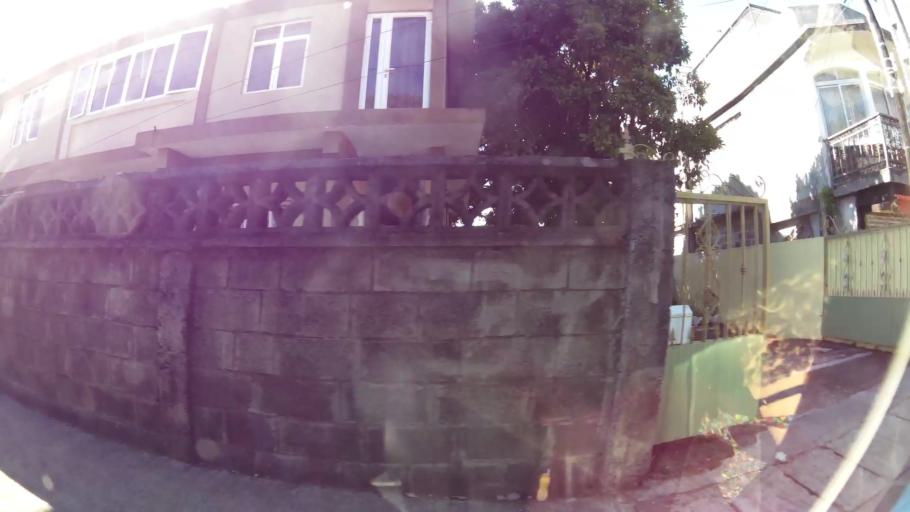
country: MU
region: Plaines Wilhems
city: Vacoas
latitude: -20.3242
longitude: 57.4853
